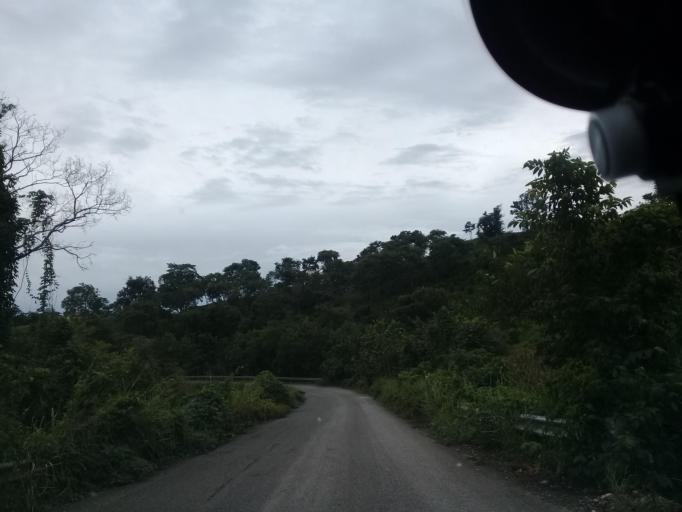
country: MX
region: Hidalgo
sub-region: Huejutla de Reyes
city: Chalahuiyapa
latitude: 21.2003
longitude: -98.3499
